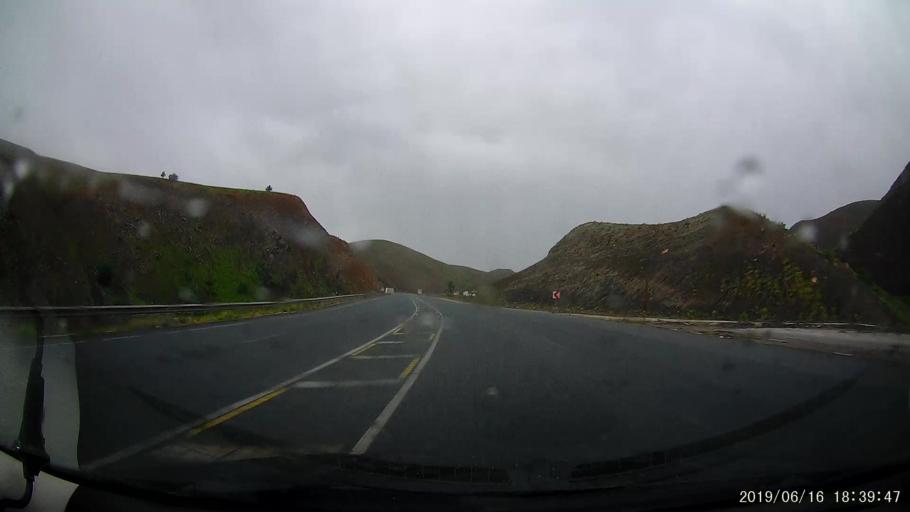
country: TR
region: Erzincan
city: Catalarmut
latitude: 39.8825
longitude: 39.1597
